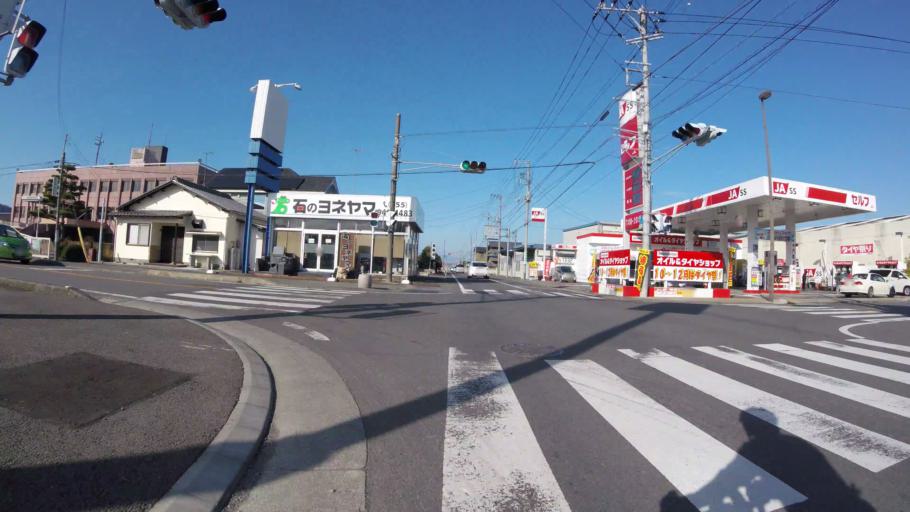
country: JP
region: Shizuoka
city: Mishima
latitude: 35.0587
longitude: 138.9536
